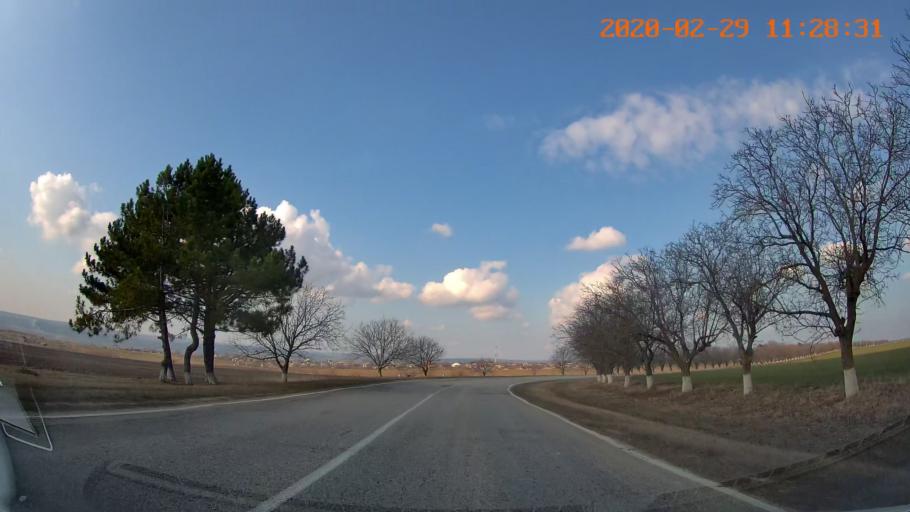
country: MD
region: Telenesti
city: Cocieri
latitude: 47.4816
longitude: 29.1340
